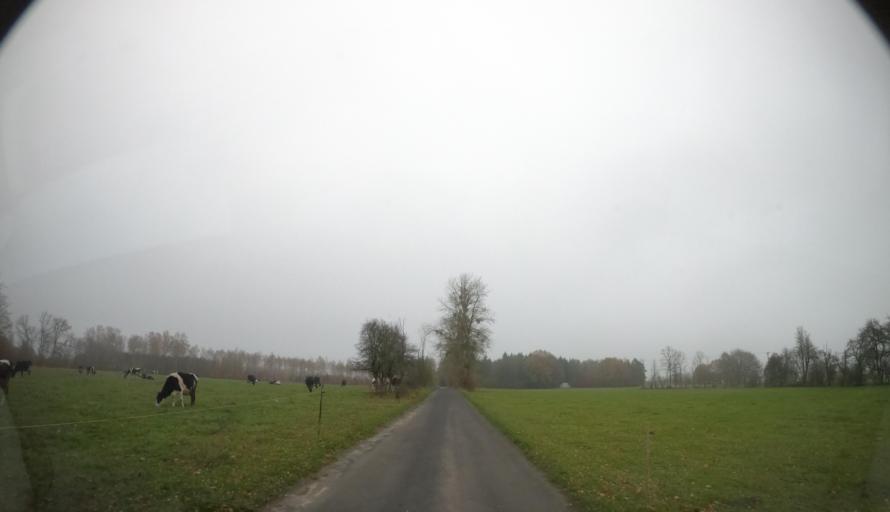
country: PL
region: West Pomeranian Voivodeship
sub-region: Powiat lobeski
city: Radowo Male
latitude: 53.6761
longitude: 15.4518
